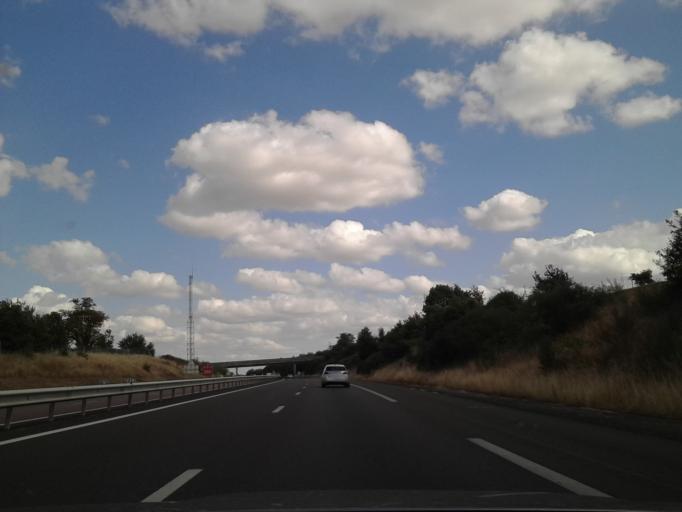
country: FR
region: Auvergne
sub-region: Departement de l'Allier
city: Vallon-en-Sully
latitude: 46.5000
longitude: 2.6466
